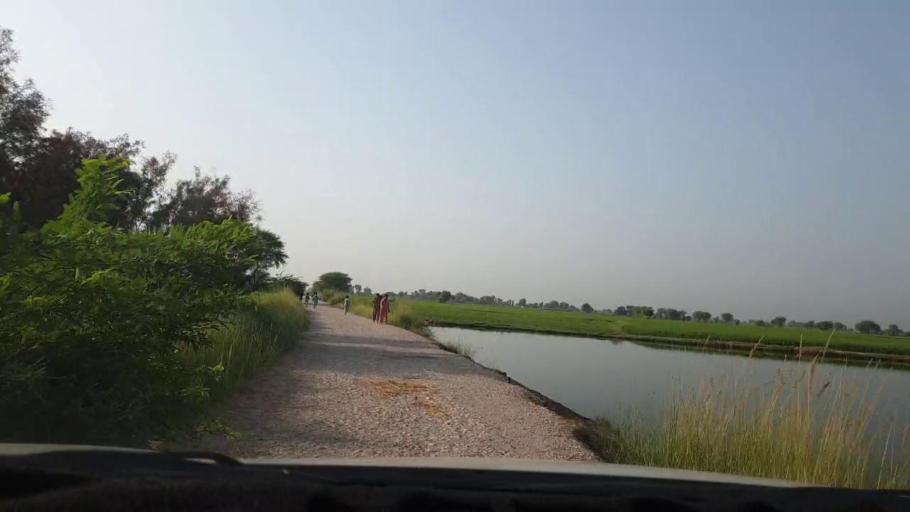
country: PK
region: Sindh
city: Larkana
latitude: 27.5096
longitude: 68.1722
